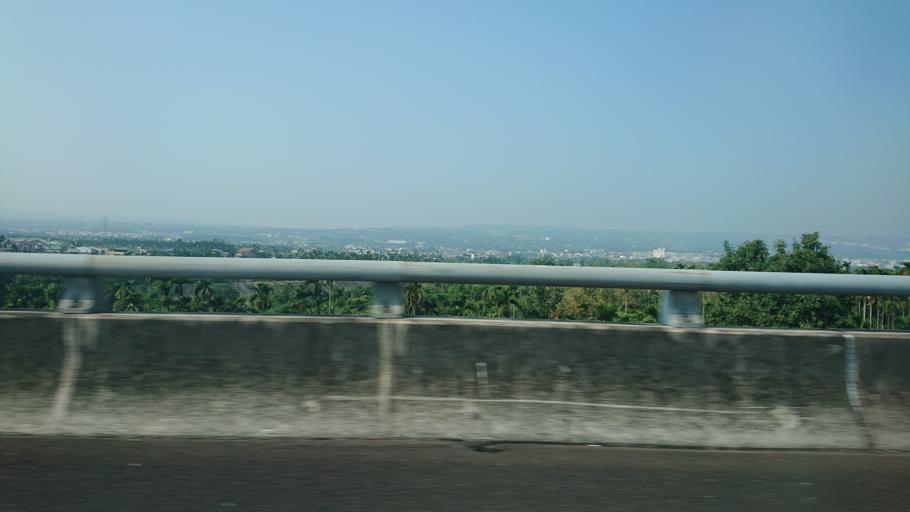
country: TW
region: Taiwan
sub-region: Nantou
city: Nantou
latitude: 23.8958
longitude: 120.7108
